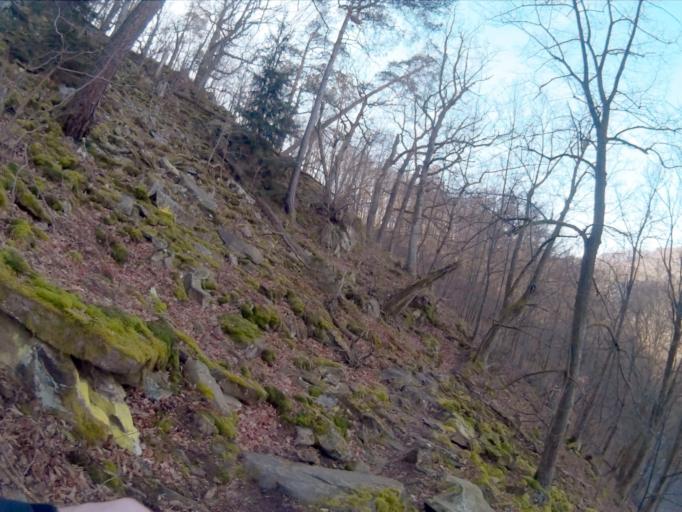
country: CZ
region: Vysocina
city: Namest' nad Oslavou
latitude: 49.1594
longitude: 16.1681
